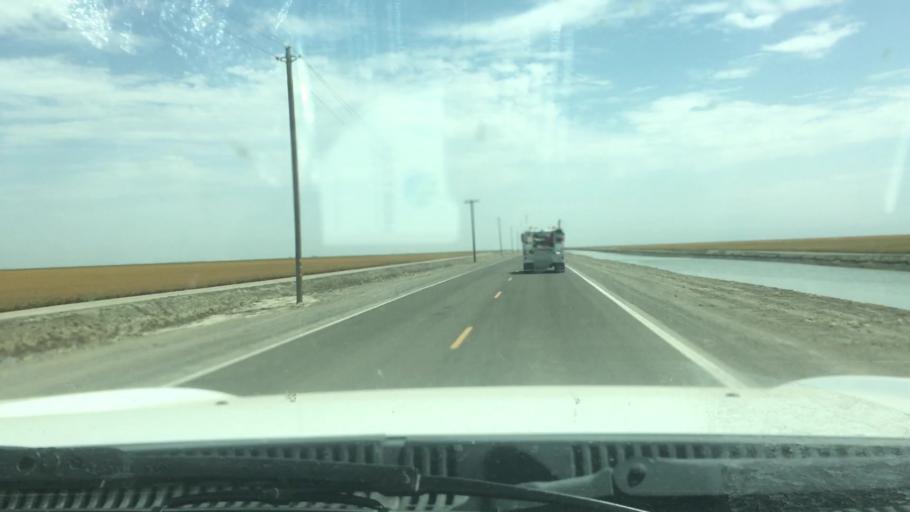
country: US
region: California
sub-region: Tulare County
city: Alpaugh
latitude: 35.9249
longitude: -119.5733
